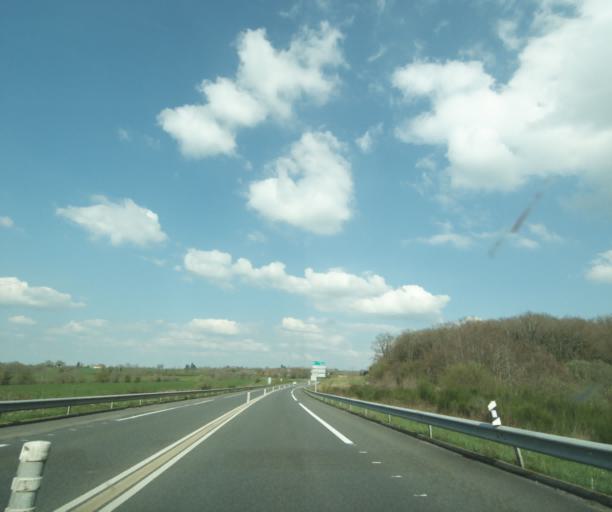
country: FR
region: Auvergne
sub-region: Departement de l'Allier
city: Buxieres-les-Mines
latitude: 46.3963
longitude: 3.0380
